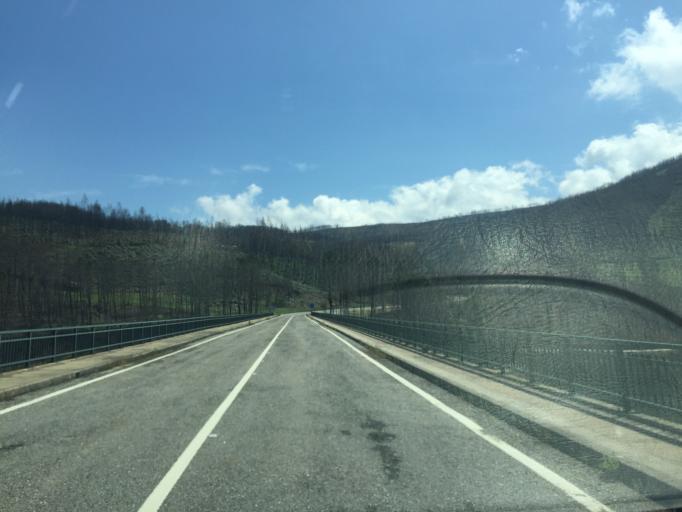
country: PT
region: Coimbra
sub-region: Pampilhosa da Serra
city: Pampilhosa da Serra
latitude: 39.9792
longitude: -7.9631
